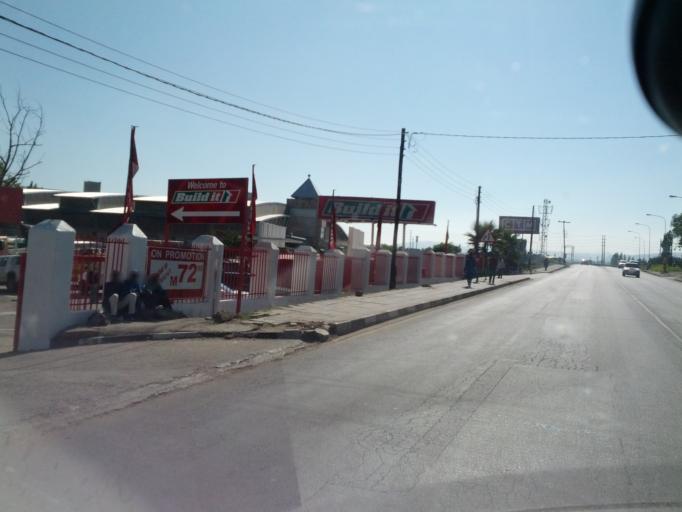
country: LS
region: Maseru
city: Maseru
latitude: -29.2987
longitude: 27.4773
